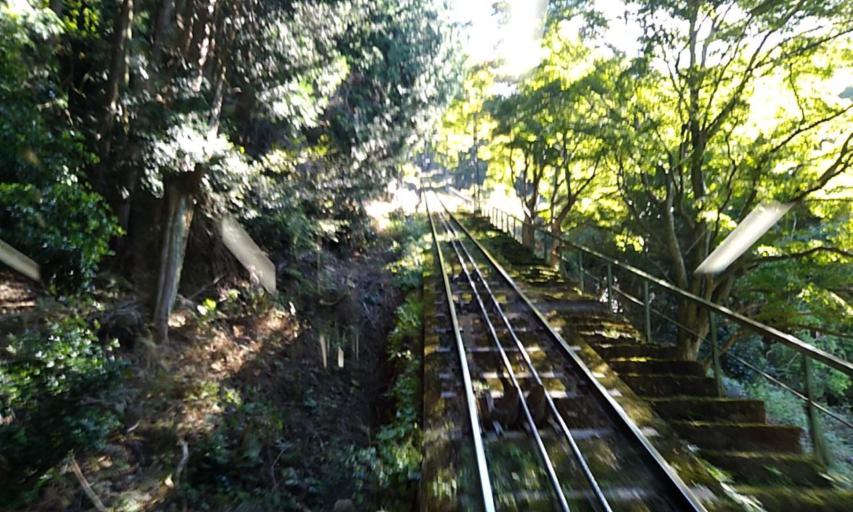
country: JP
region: Kyoto
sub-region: Kyoto-shi
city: Kamigyo-ku
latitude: 35.0649
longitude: 135.8183
